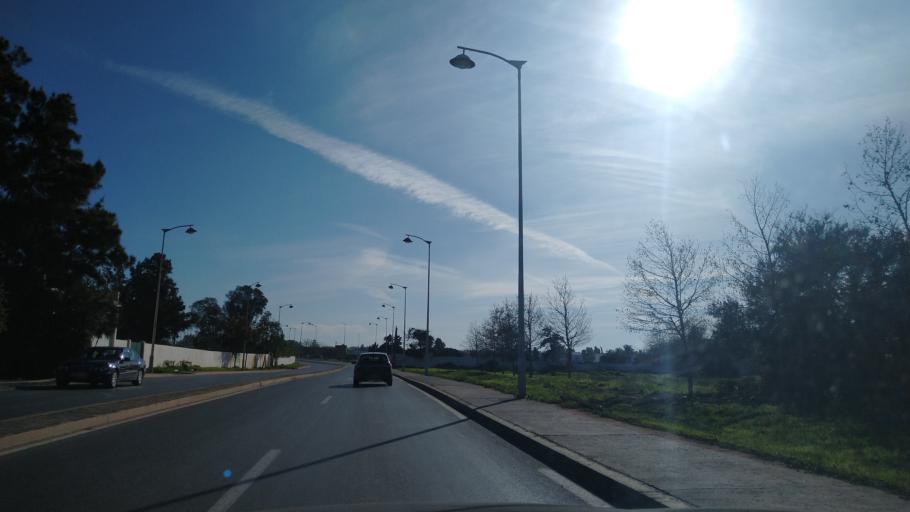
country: MA
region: Rabat-Sale-Zemmour-Zaer
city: Sale
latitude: 34.0260
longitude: -6.7352
